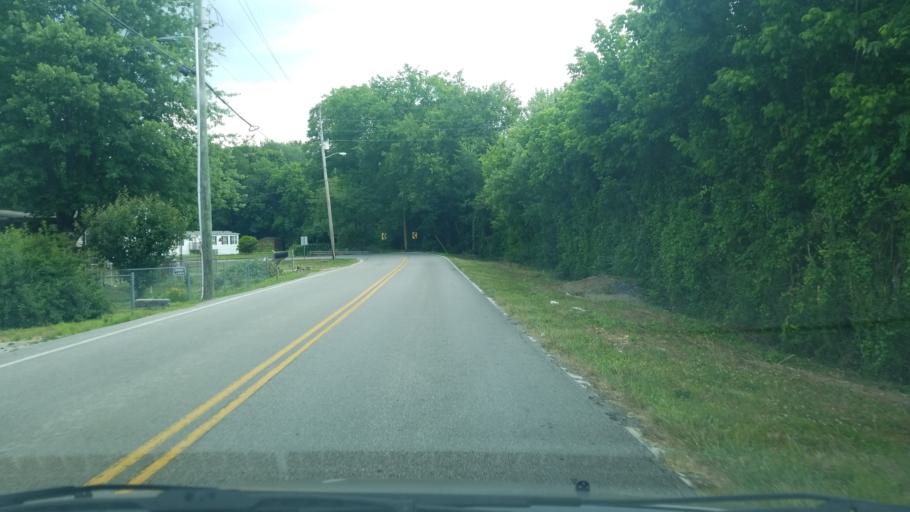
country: US
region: Tennessee
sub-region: Hamilton County
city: Soddy-Daisy
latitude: 35.2425
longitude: -85.1863
